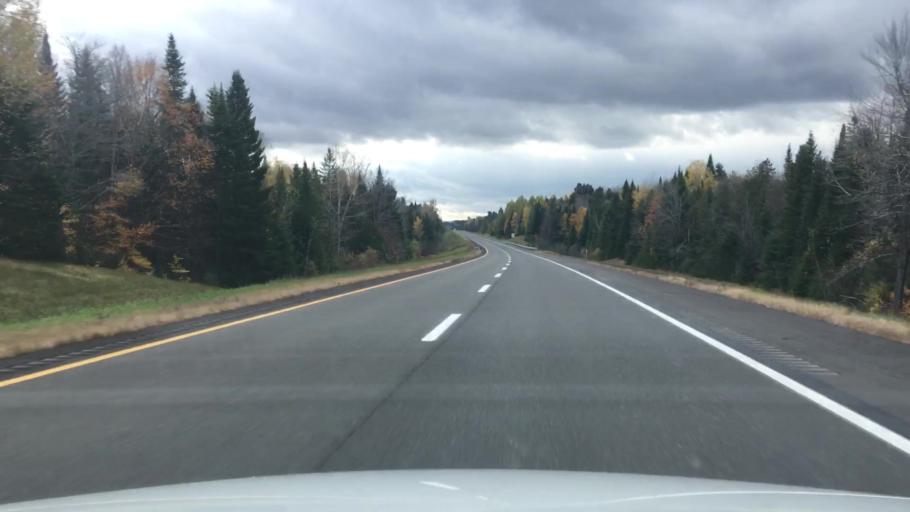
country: US
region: Maine
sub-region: Penobscot County
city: Patten
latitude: 46.0871
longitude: -68.2074
